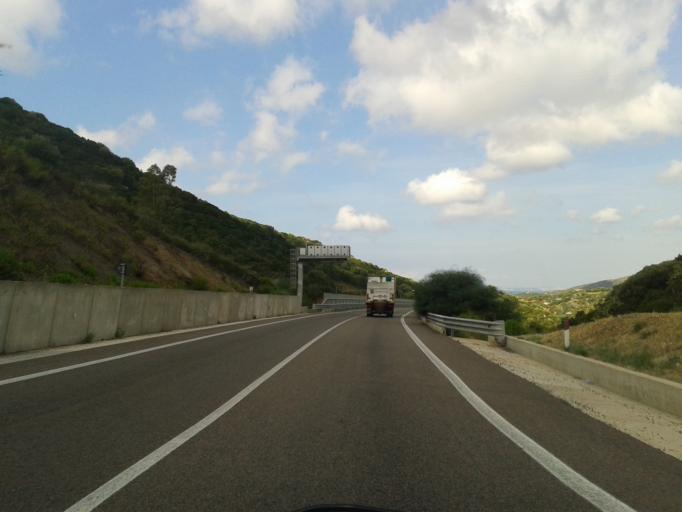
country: IT
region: Sardinia
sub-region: Provincia di Cagliari
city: Villasimius
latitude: 39.1733
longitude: 9.4387
